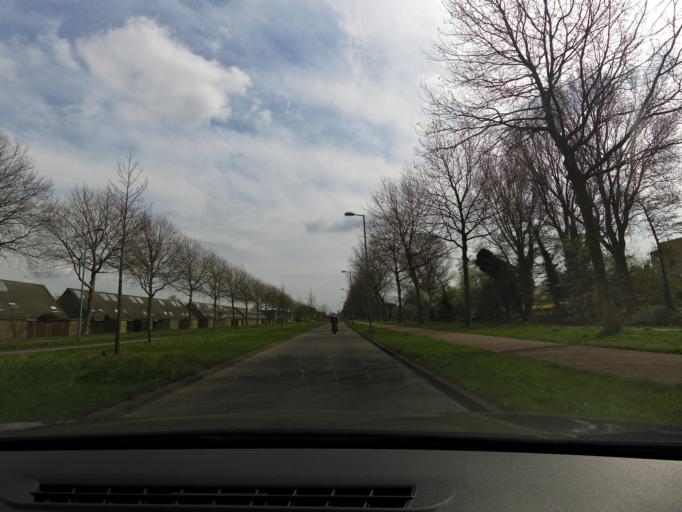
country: NL
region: South Holland
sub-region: Gemeente Spijkenisse
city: Spijkenisse
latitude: 51.8562
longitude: 4.3670
